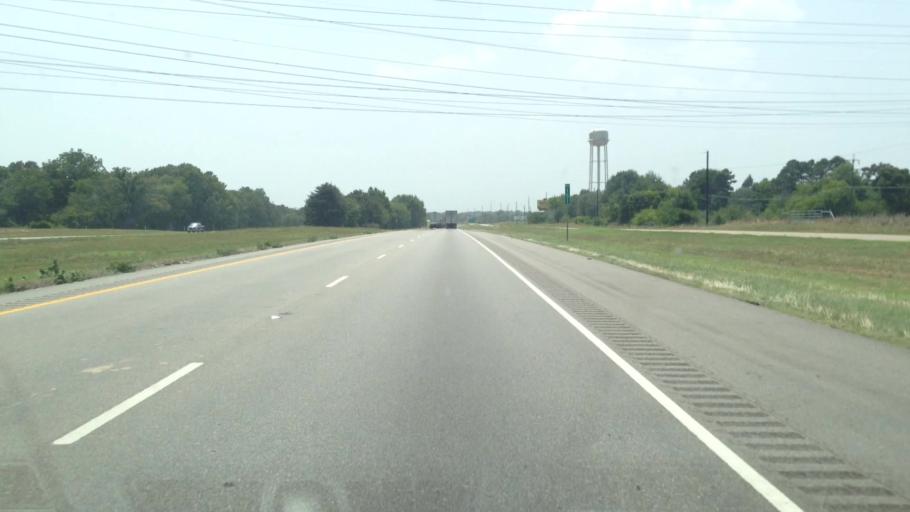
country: US
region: Texas
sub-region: Franklin County
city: Mount Vernon
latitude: 33.1626
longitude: -95.1628
